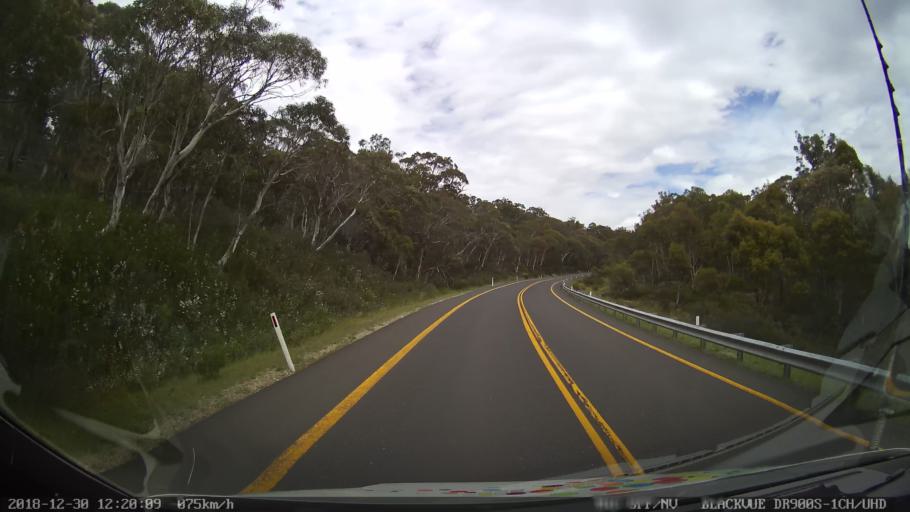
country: AU
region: New South Wales
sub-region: Snowy River
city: Jindabyne
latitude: -36.3463
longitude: 148.5334
